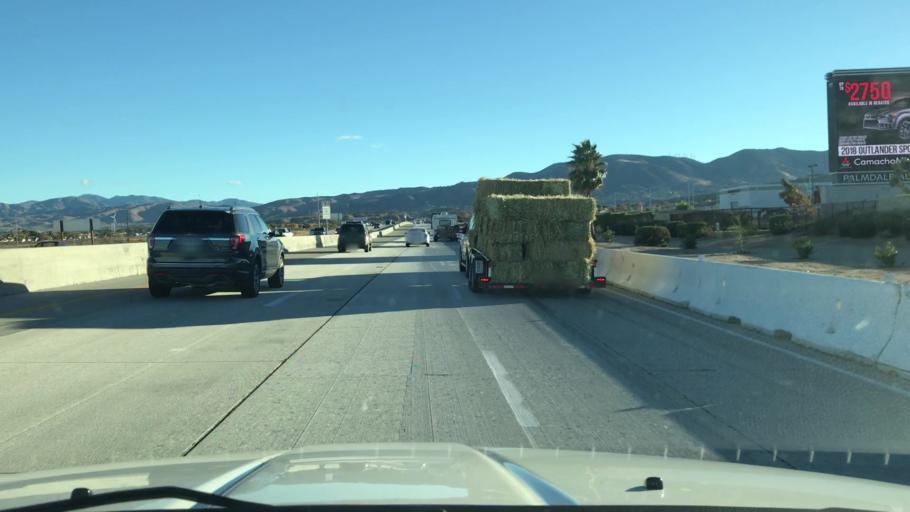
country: US
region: California
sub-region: Los Angeles County
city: Desert View Highlands
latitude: 34.5911
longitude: -118.1346
